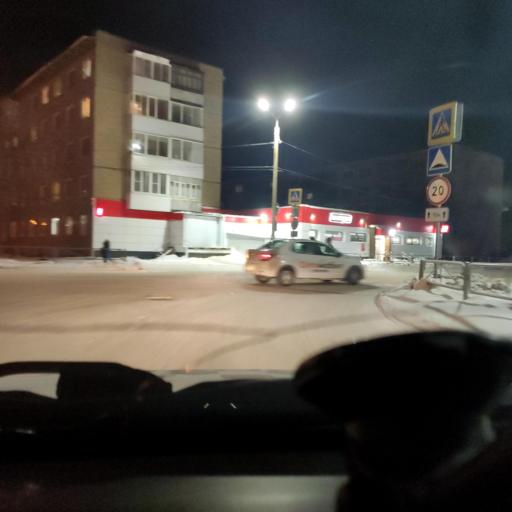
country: RU
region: Perm
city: Krasnokamsk
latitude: 58.0884
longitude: 55.7573
